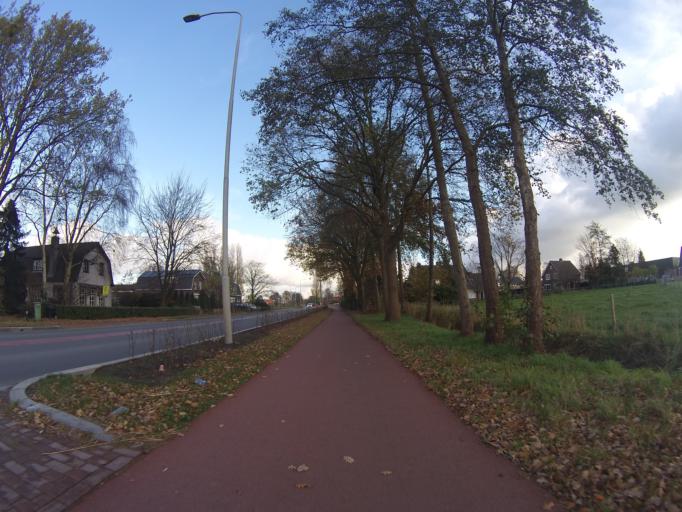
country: NL
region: Gelderland
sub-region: Gemeente Nijkerk
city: Nijkerk
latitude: 52.2013
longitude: 5.4597
